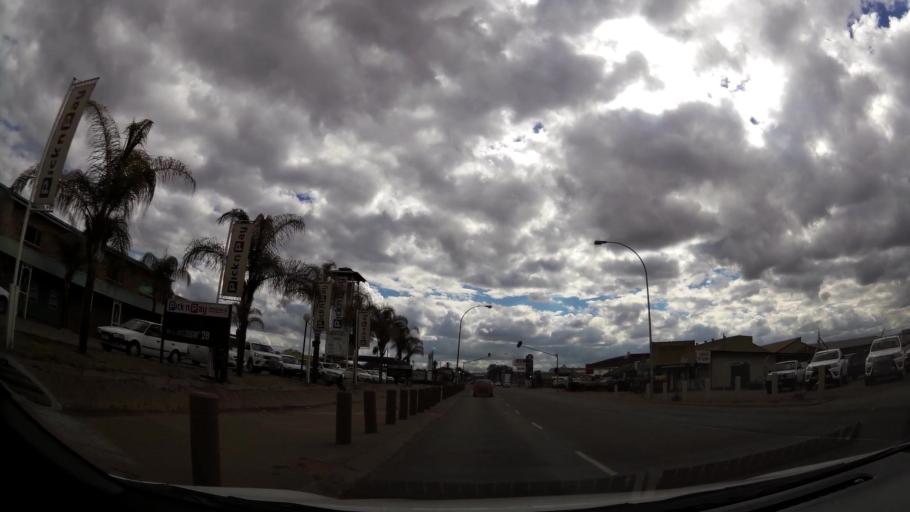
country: ZA
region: Limpopo
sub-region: Waterberg District Municipality
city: Modimolle
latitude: -24.7113
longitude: 28.4161
